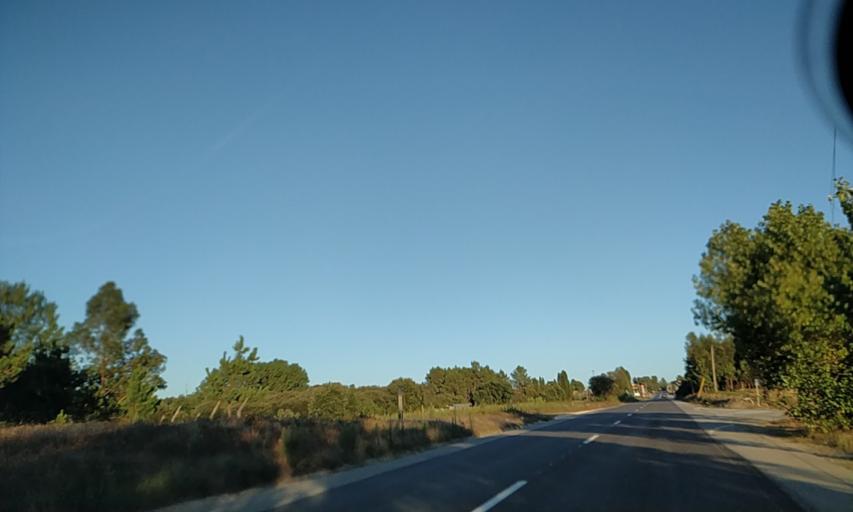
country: PT
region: Aveiro
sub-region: Oliveira do Bairro
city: Oia
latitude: 40.5536
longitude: -8.5489
